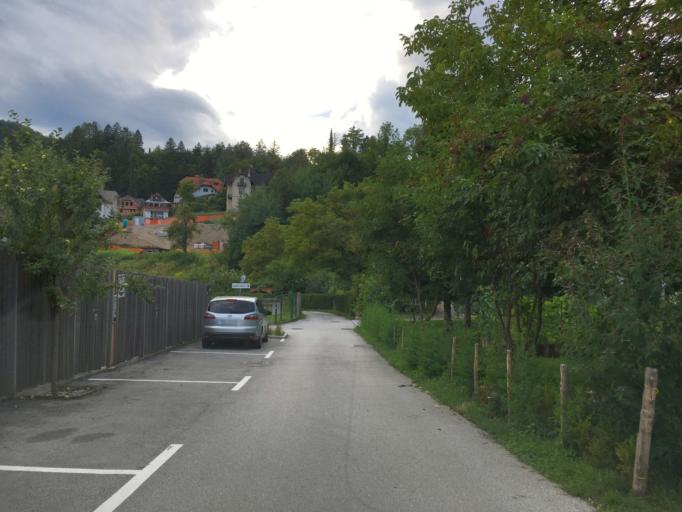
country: SI
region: Bled
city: Bled
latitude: 46.3579
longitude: 14.0973
